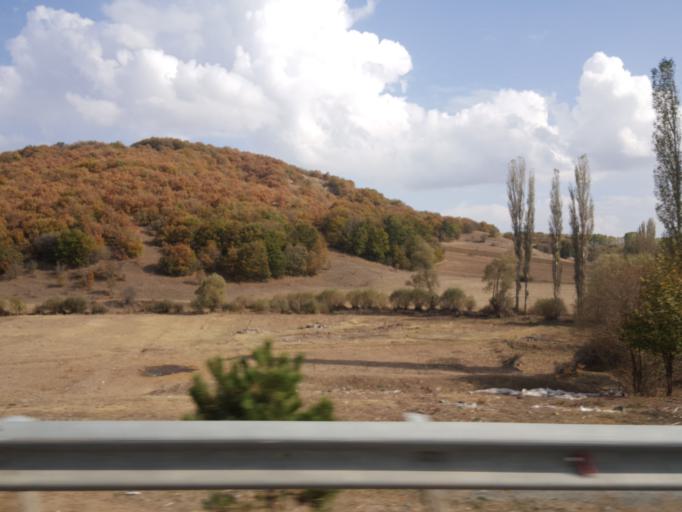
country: TR
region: Corum
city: Alaca
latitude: 40.3054
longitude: 34.6555
